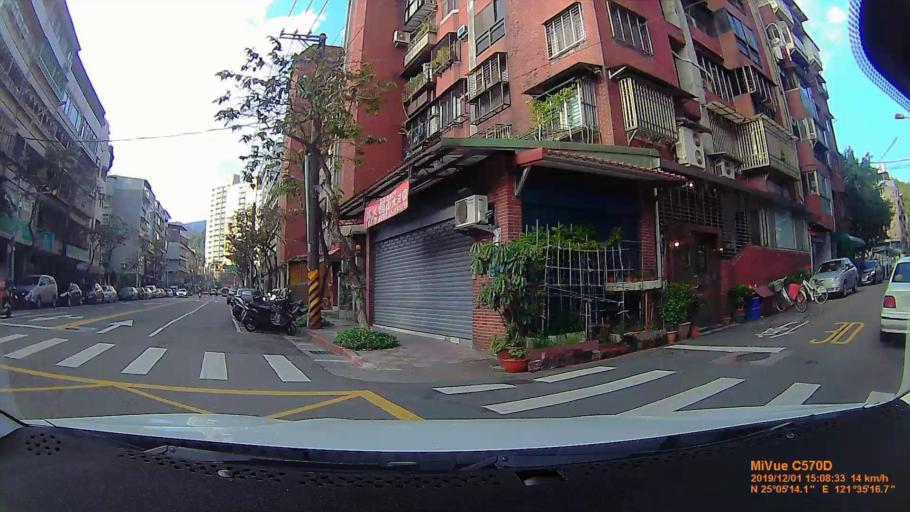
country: TW
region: Taipei
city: Taipei
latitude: 25.0873
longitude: 121.5880
